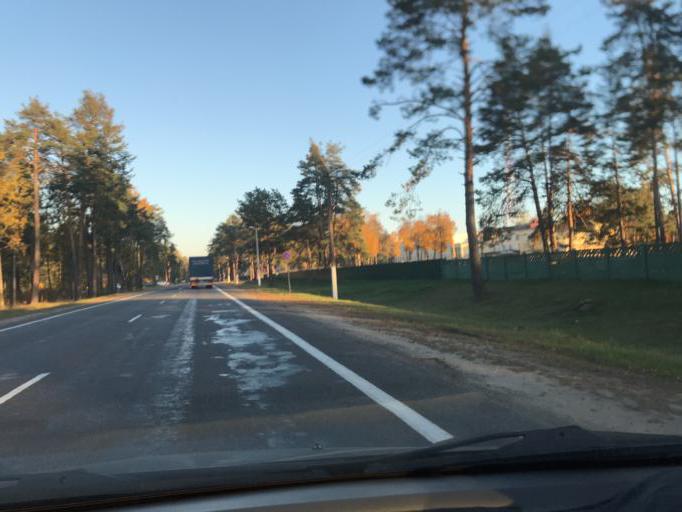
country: BY
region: Minsk
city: Staryya Darohi
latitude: 53.0355
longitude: 28.2261
